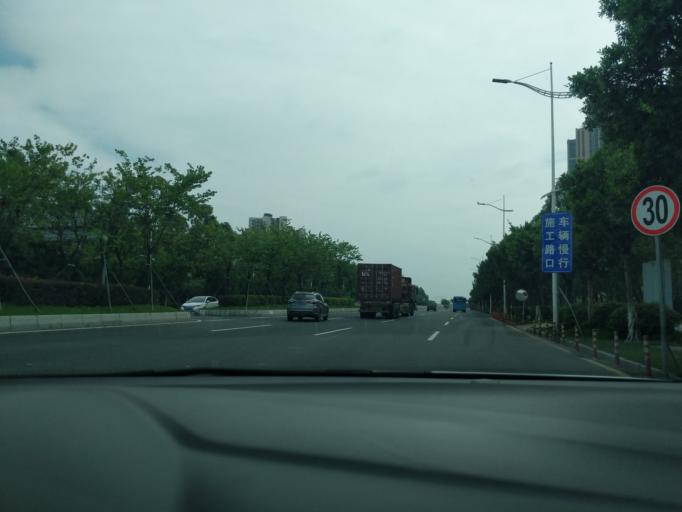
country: CN
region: Guangdong
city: Nansha
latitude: 22.7506
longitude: 113.5812
